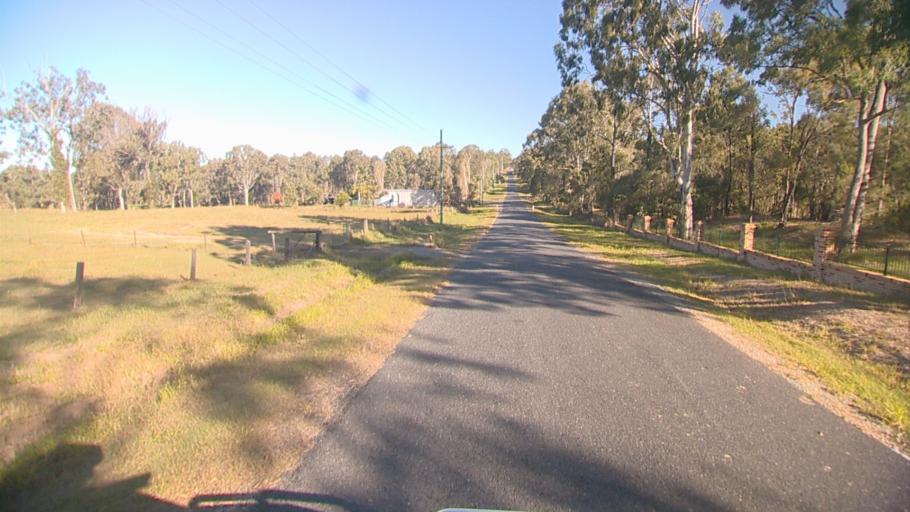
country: AU
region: Queensland
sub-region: Logan
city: Logan Reserve
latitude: -27.7196
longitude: 153.1064
